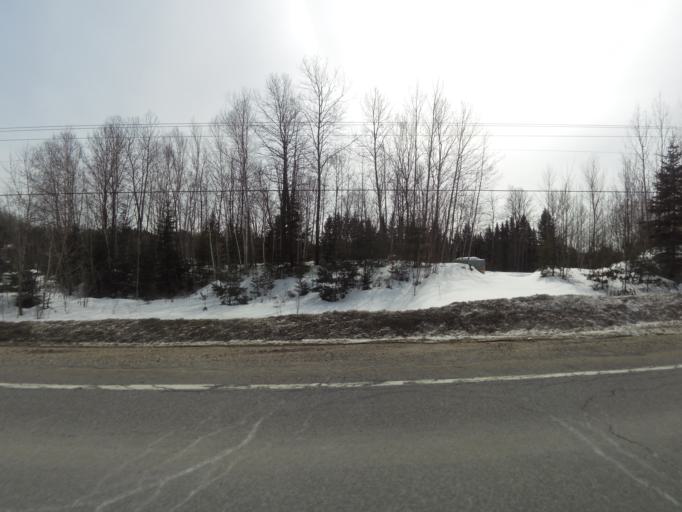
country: CA
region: Quebec
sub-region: Outaouais
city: Val-des-Monts
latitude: 45.9928
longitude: -75.5639
